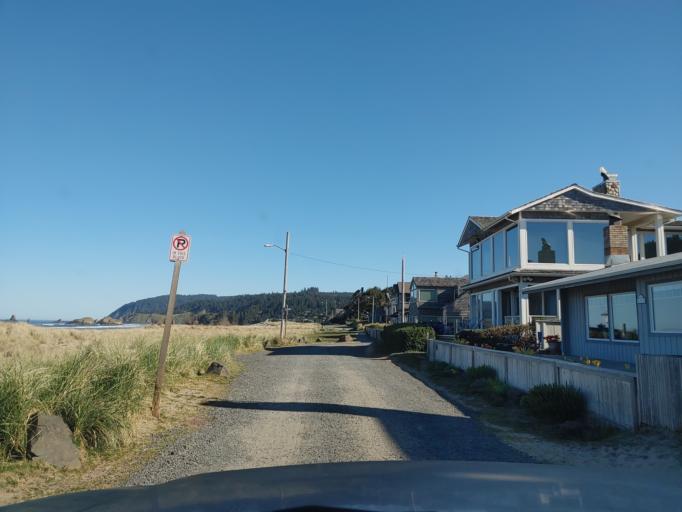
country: US
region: Oregon
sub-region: Clatsop County
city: Cannon Beach
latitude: 45.8935
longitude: -123.9634
